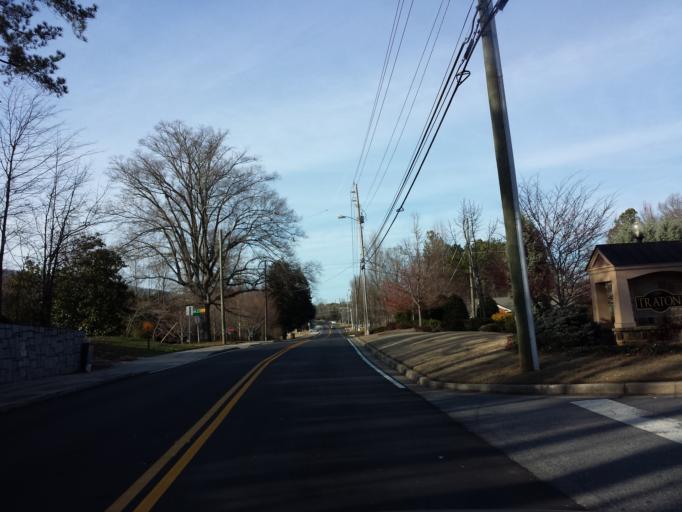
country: US
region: Georgia
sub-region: Cobb County
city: Marietta
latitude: 33.9704
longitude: -84.5635
